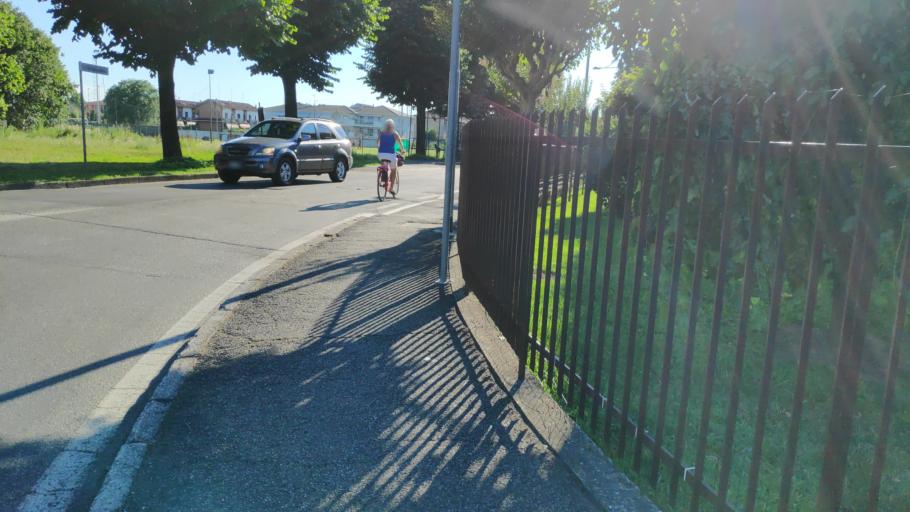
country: IT
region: Lombardy
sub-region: Citta metropolitana di Milano
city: Pozzuolo Martesana
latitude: 45.5137
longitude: 9.4606
